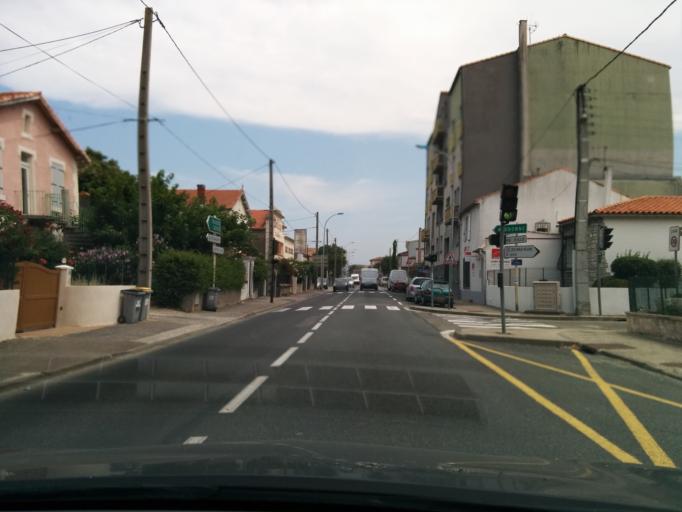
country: FR
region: Languedoc-Roussillon
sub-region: Departement de l'Aude
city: Carcassonne
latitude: 43.2219
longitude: 2.3381
